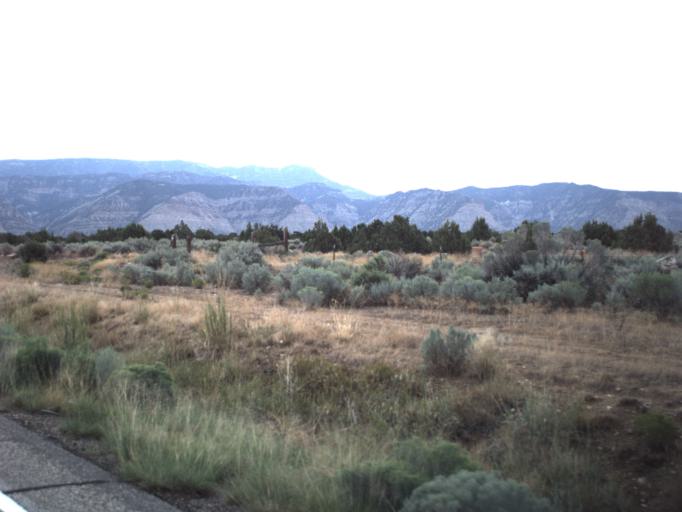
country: US
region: Utah
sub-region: Carbon County
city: East Carbon City
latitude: 39.5397
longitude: -110.4352
